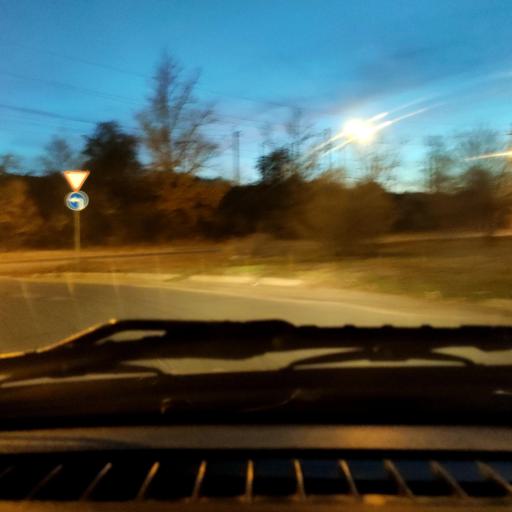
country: RU
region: Samara
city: Zhigulevsk
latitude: 53.4722
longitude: 49.5402
